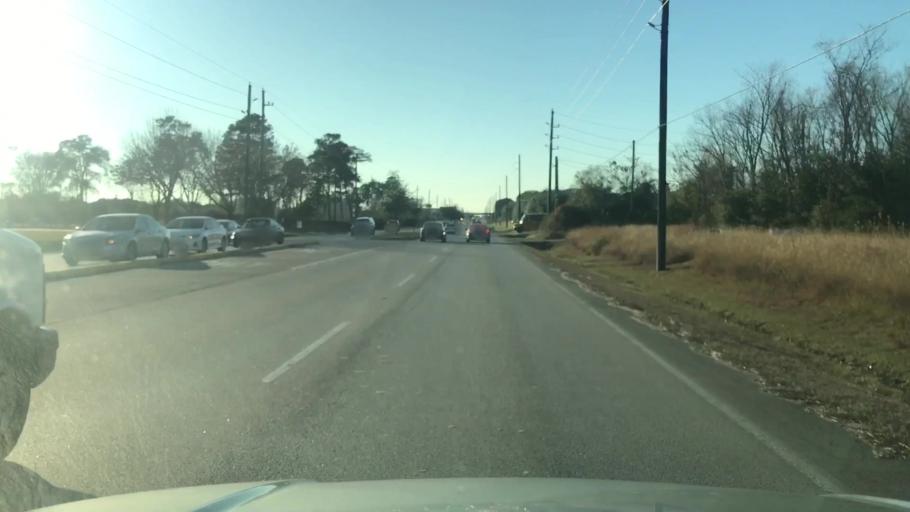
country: US
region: Texas
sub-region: Harris County
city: Katy
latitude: 29.8318
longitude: -95.7470
